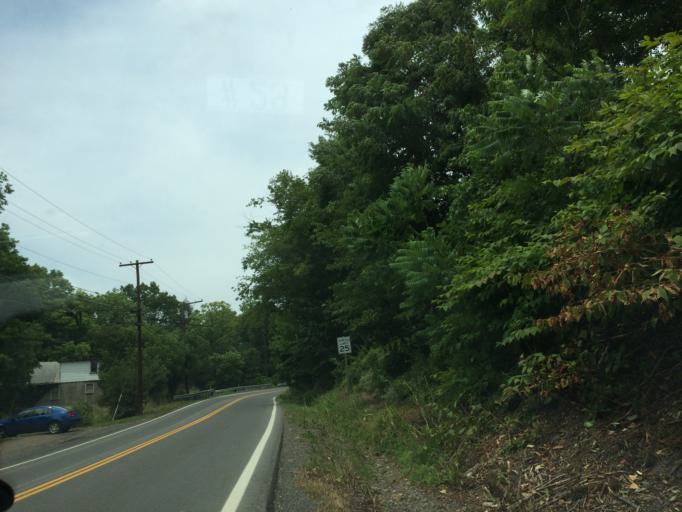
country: US
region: Maryland
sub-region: Allegany County
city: Westernport
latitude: 39.5250
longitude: -79.0184
